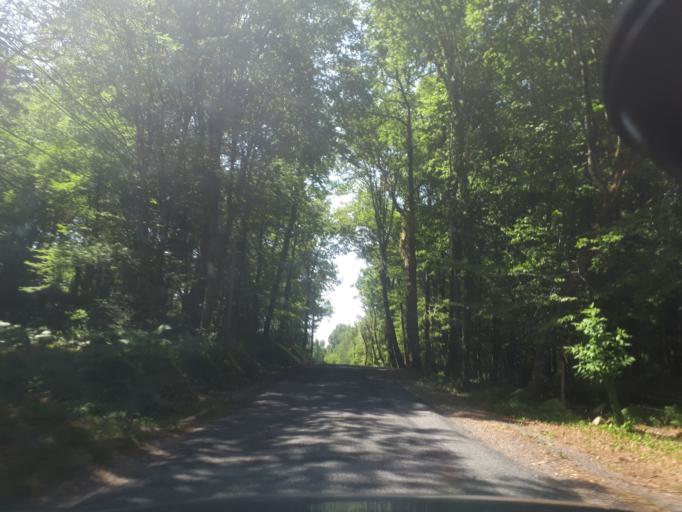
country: FR
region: Midi-Pyrenees
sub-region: Departement du Lot
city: Gourdon
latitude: 44.7690
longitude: 1.3589
